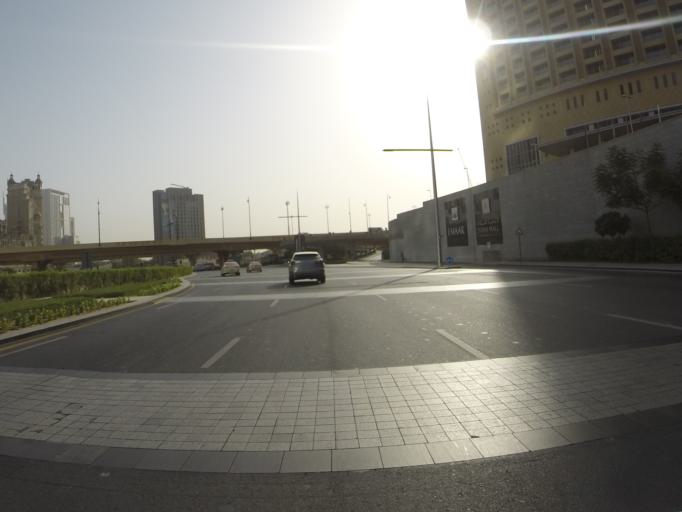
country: AE
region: Dubai
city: Dubai
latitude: 25.1999
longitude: 55.2766
